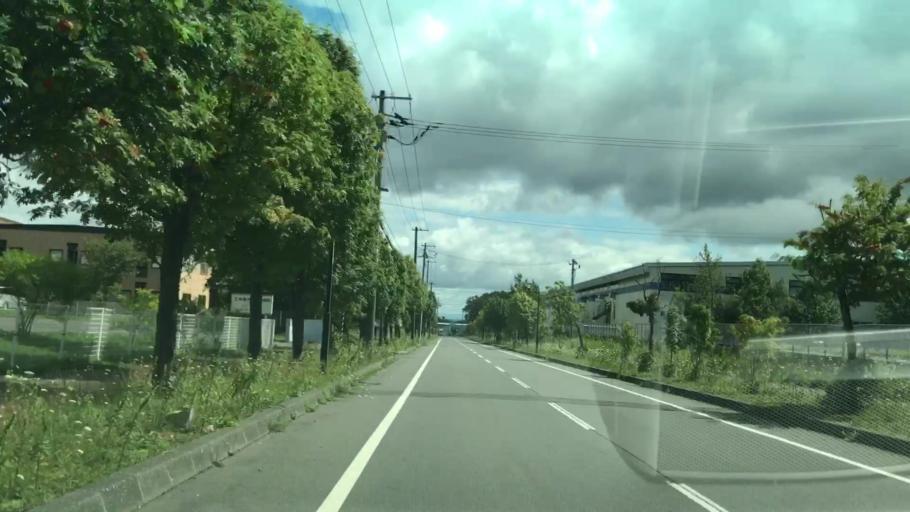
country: JP
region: Hokkaido
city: Chitose
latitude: 42.7775
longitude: 141.6128
